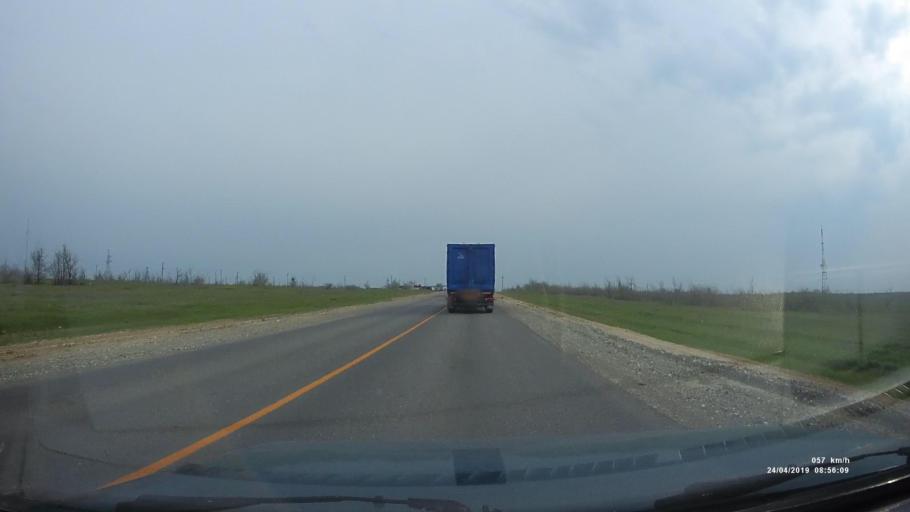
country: RU
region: Kalmykiya
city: Arshan'
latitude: 46.2999
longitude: 44.1825
